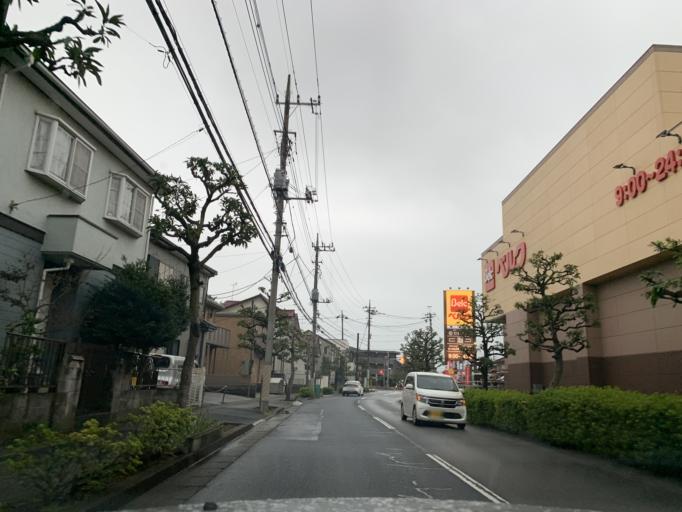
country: JP
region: Chiba
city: Nagareyama
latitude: 35.9104
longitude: 139.9105
